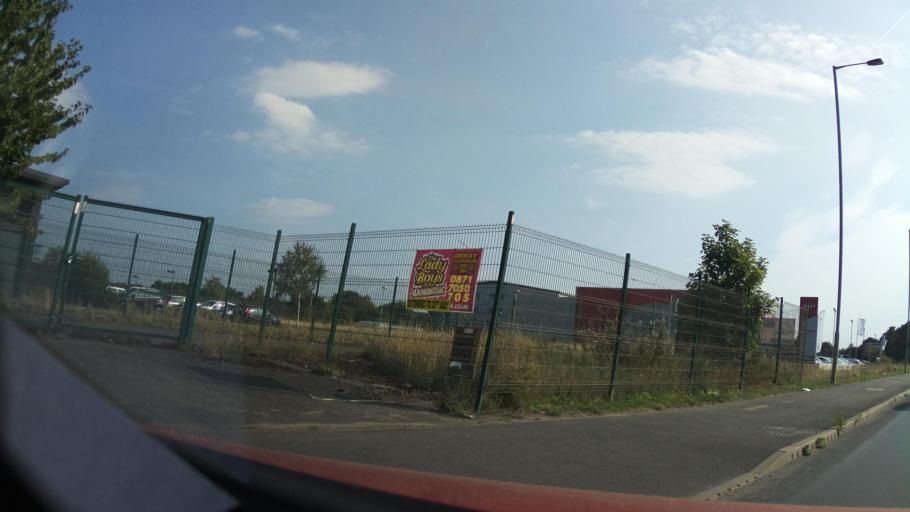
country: GB
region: England
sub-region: Staffordshire
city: Burton upon Trent
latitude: 52.7914
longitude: -1.6707
